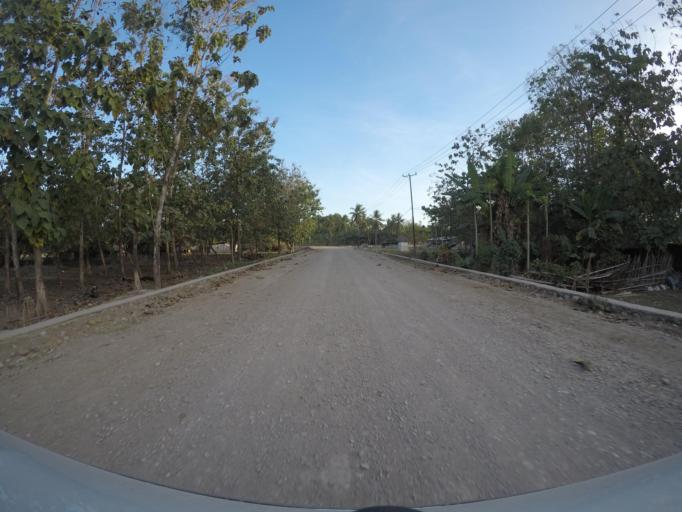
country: TL
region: Viqueque
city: Viqueque
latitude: -8.8726
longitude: 126.5074
